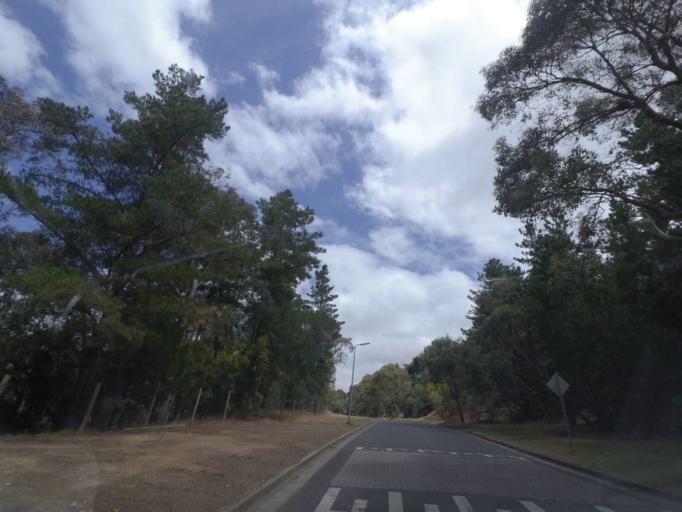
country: AU
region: Victoria
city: Mitcham
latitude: -37.7996
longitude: 145.2126
